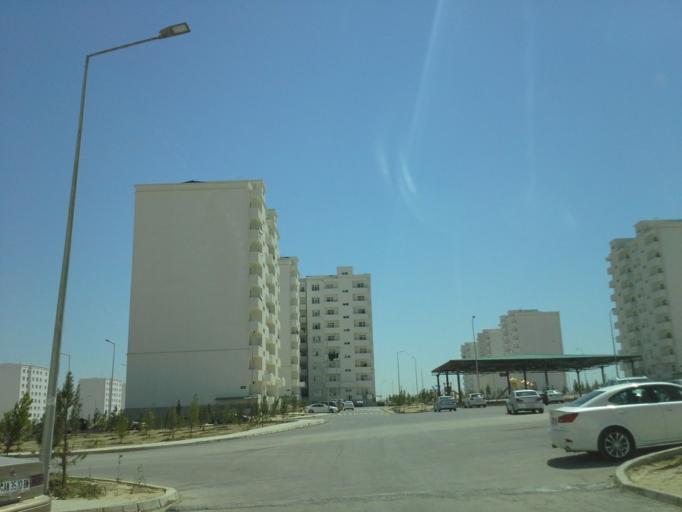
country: TM
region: Ahal
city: Ashgabat
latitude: 37.8893
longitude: 58.4071
